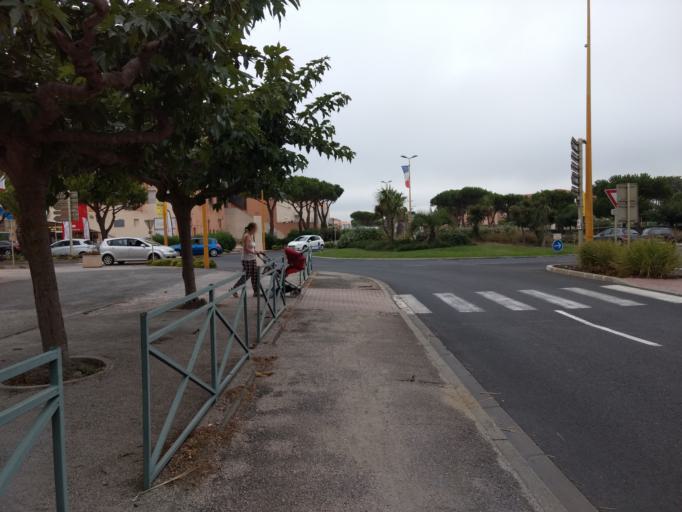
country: FR
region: Languedoc-Roussillon
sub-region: Departement des Pyrenees-Orientales
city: Le Barcares
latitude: 42.7918
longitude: 3.0355
